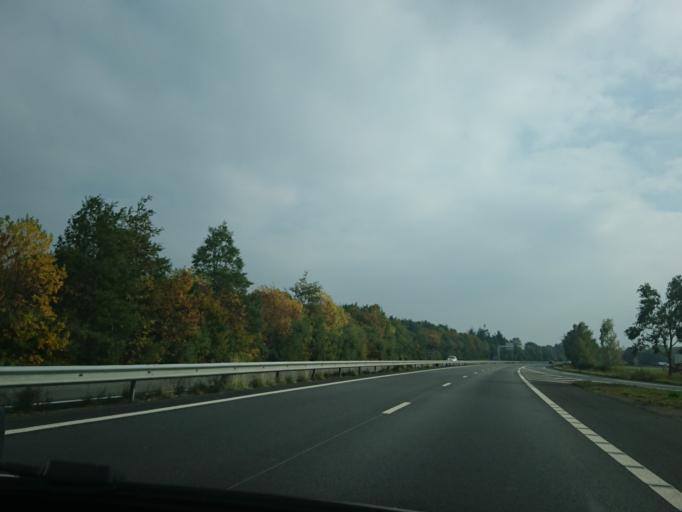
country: FR
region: Pays de la Loire
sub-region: Departement de la Loire-Atlantique
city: Derval
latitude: 47.6479
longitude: -1.6603
